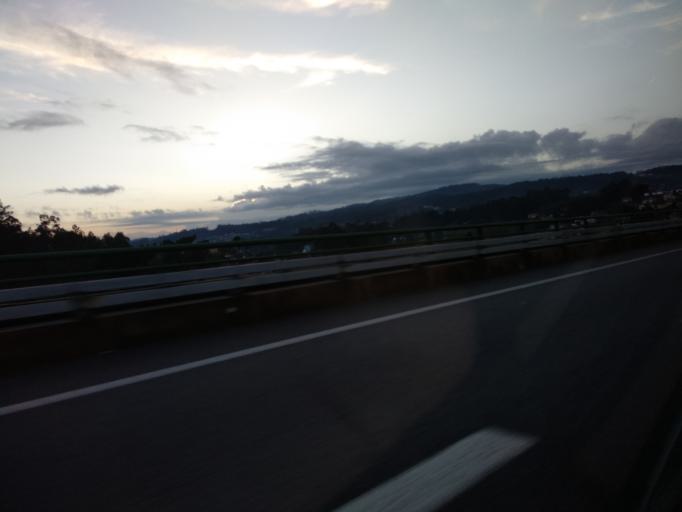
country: PT
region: Braga
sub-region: Braga
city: Oliveira
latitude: 41.4988
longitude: -8.4708
